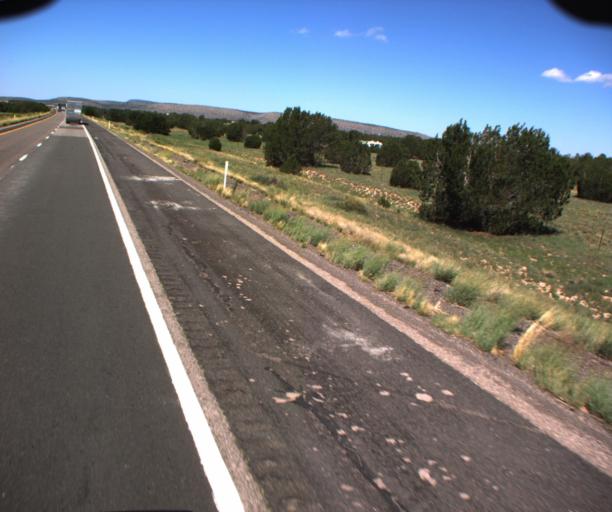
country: US
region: Arizona
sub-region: Mohave County
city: Peach Springs
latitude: 35.3219
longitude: -112.9386
